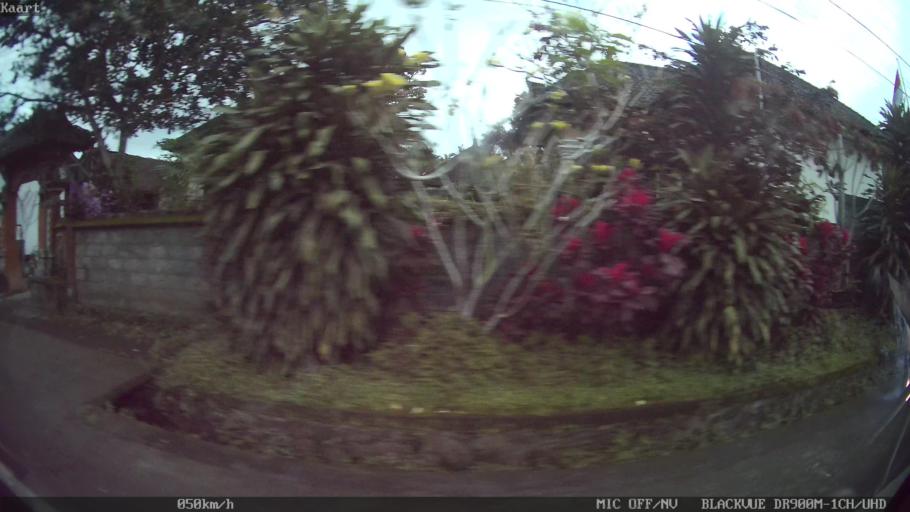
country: ID
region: Bali
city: Banjar Wangsian
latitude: -8.4284
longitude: 115.4312
